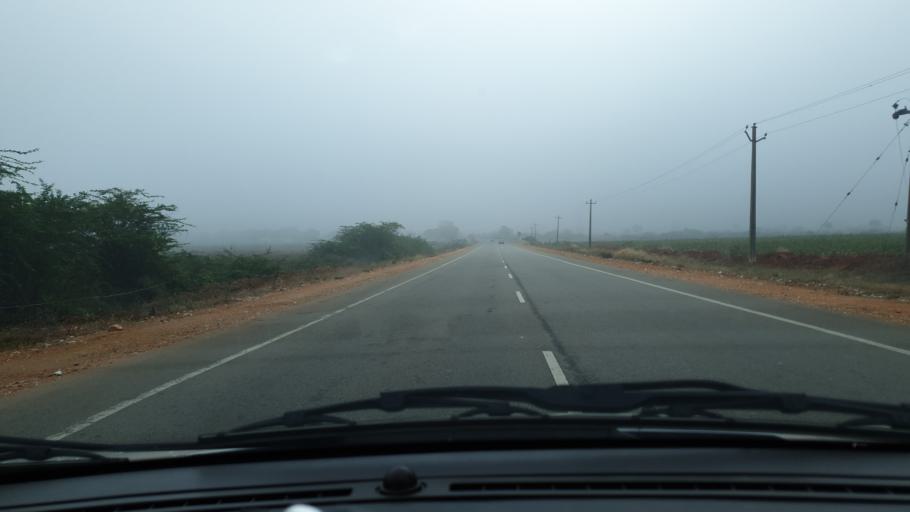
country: IN
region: Telangana
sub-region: Mahbubnagar
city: Nagar Karnul
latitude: 16.6324
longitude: 78.6067
